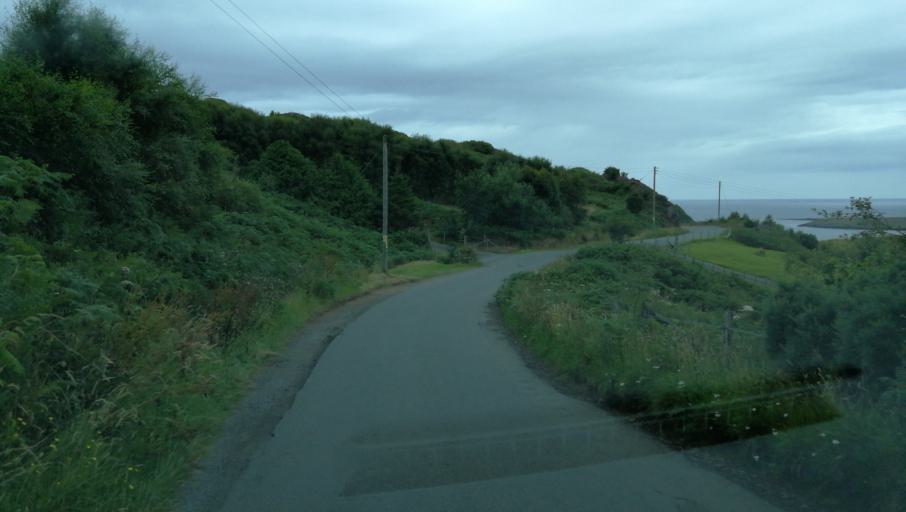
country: GB
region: Scotland
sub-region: Highland
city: Portree
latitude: 57.6478
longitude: -6.2441
